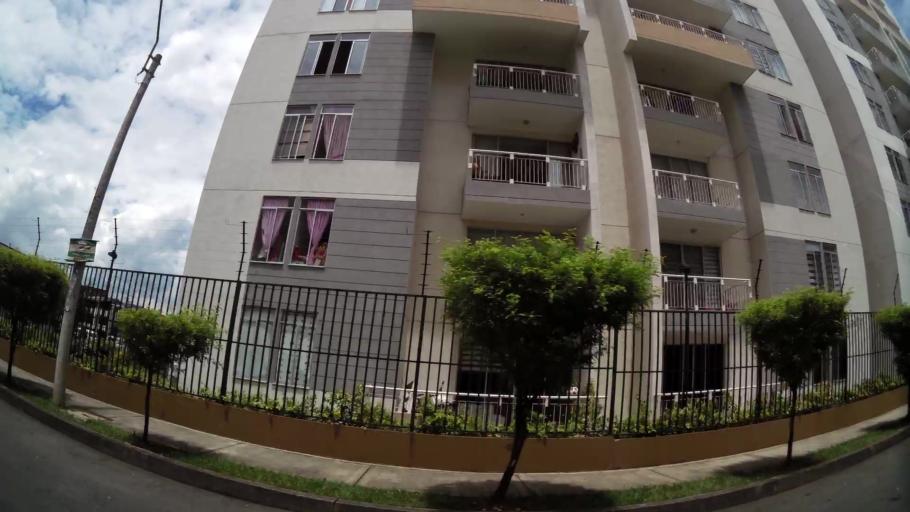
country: CO
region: Valle del Cauca
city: Cali
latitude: 3.3721
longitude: -76.5170
